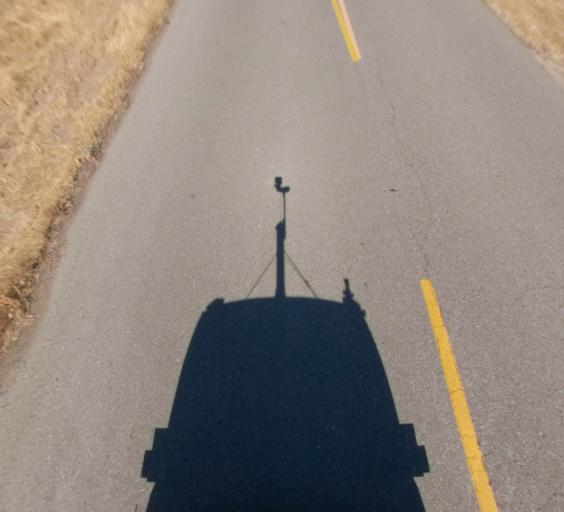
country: US
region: California
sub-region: Madera County
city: Bonadelle Ranchos-Madera Ranchos
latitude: 37.0031
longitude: -119.8676
